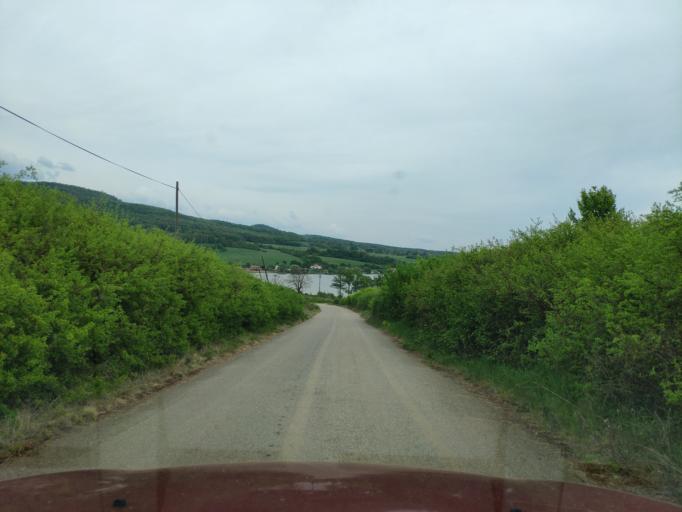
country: SK
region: Banskobystricky
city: Rimavska Sobota
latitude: 48.4837
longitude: 20.0872
